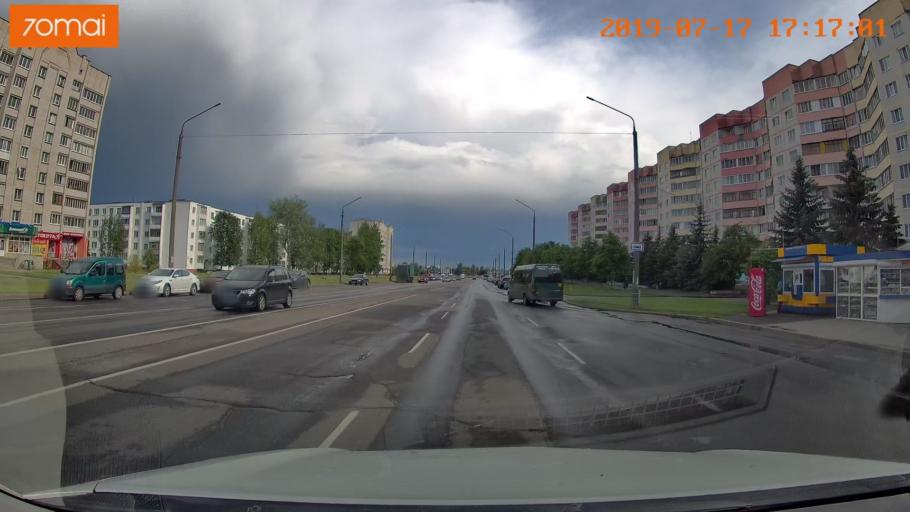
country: BY
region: Mogilev
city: Babruysk
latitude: 53.1637
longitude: 29.1967
